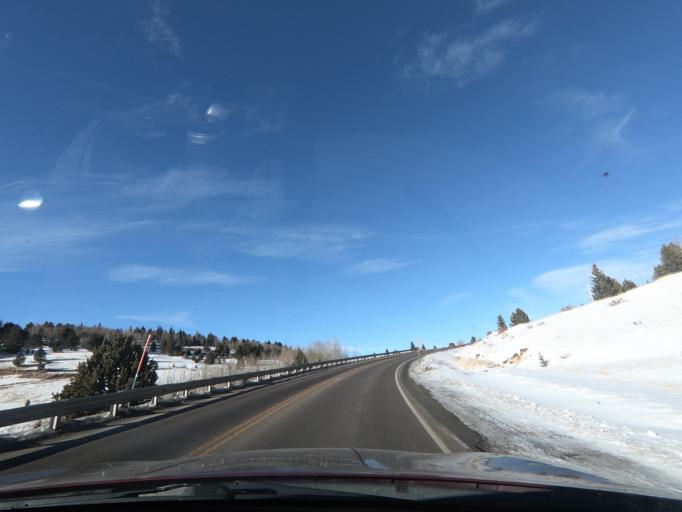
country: US
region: Colorado
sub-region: Teller County
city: Cripple Creek
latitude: 38.7606
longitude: -105.1617
